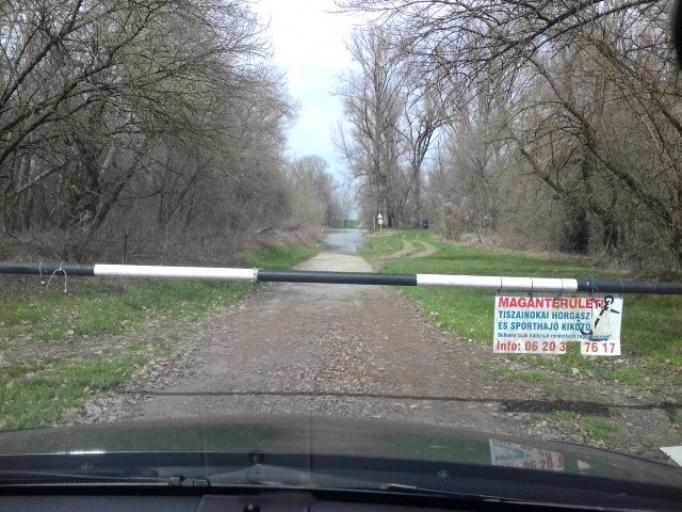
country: HU
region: Bacs-Kiskun
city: Tiszakecske
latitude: 46.9057
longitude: 20.1342
